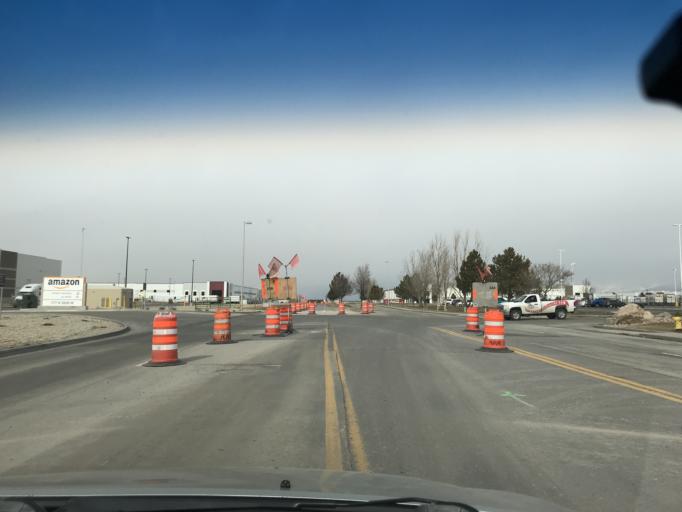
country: US
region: Utah
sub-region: Salt Lake County
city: West Valley City
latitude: 40.7847
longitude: -112.0251
